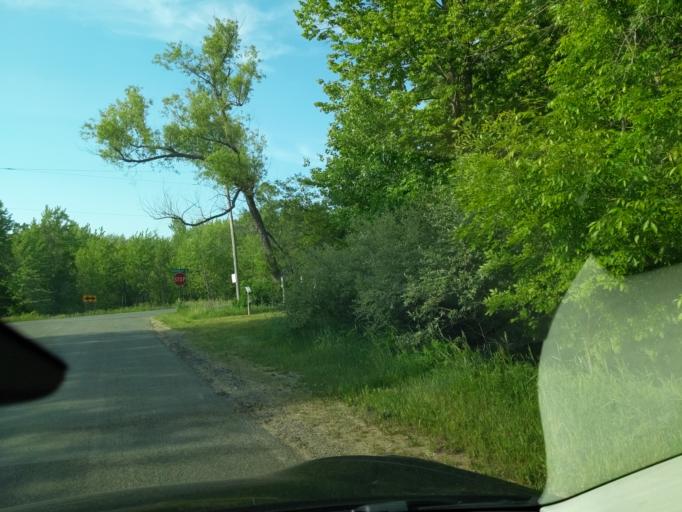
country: US
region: Michigan
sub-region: Barry County
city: Nashville
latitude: 42.6227
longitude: -85.1536
